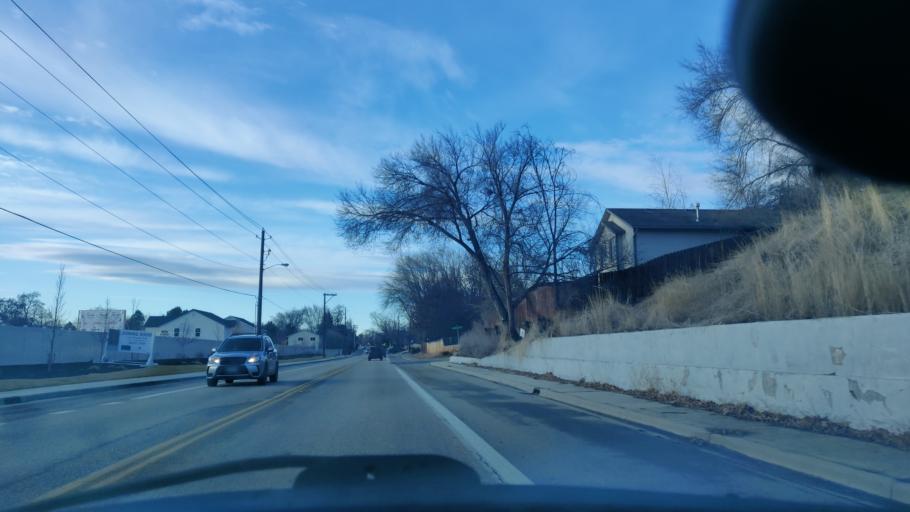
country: US
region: Idaho
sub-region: Ada County
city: Garden City
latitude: 43.6522
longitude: -116.2284
